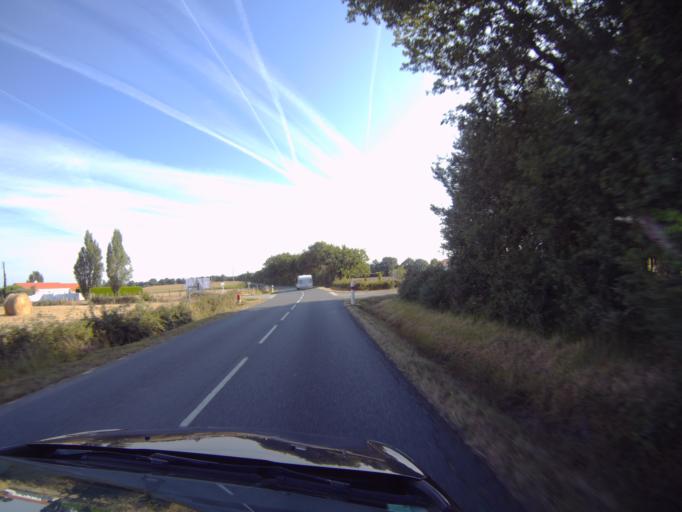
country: FR
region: Pays de la Loire
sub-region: Departement de la Vendee
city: Saint-Hilaire-de-Talmont
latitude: 46.4855
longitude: -1.5859
